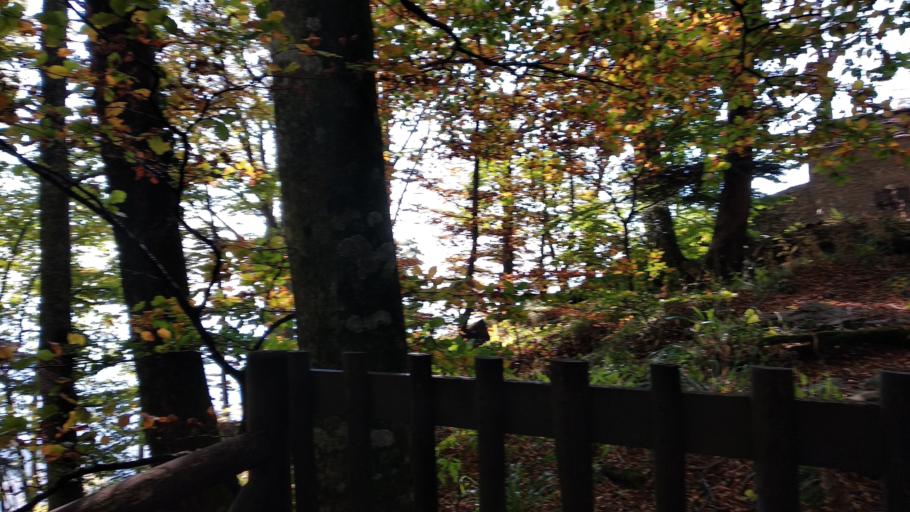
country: IT
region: Tuscany
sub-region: Province of Arezzo
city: Chiusi della Verna
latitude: 43.7080
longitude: 11.9297
